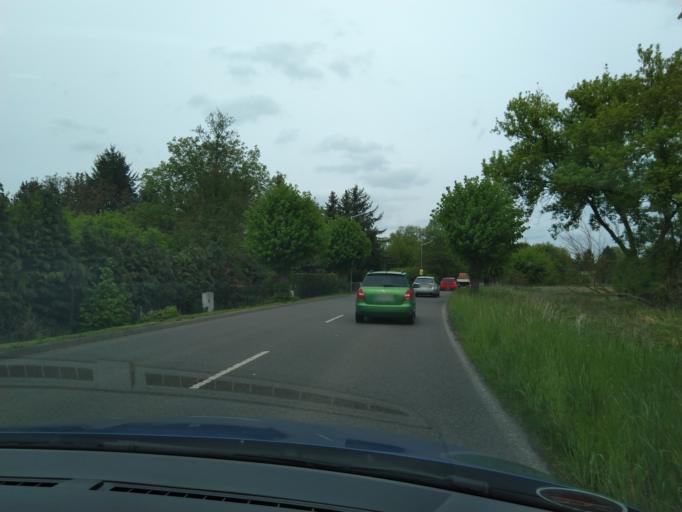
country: DE
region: Brandenburg
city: Oderberg
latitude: 52.8560
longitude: 14.0359
